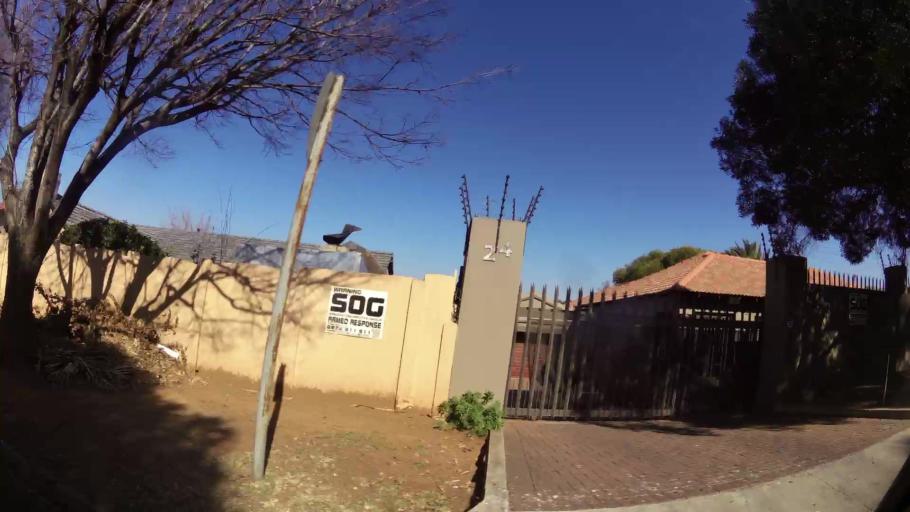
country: ZA
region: Gauteng
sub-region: Ekurhuleni Metropolitan Municipality
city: Germiston
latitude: -26.2530
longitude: 28.1126
